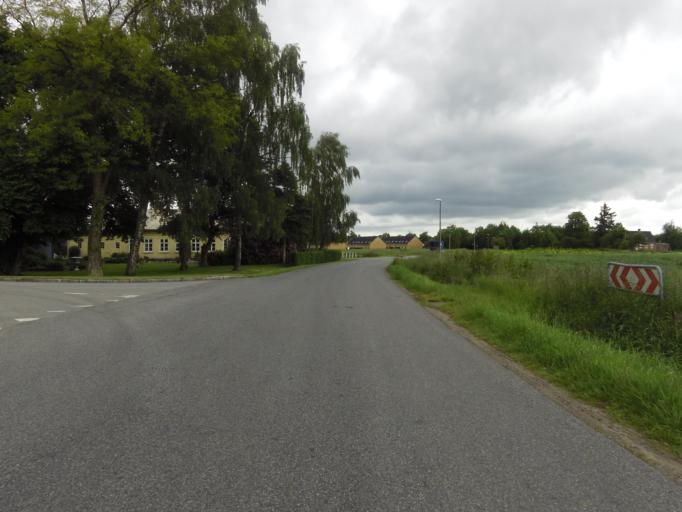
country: DK
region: South Denmark
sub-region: Haderslev Kommune
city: Gram
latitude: 55.2815
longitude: 9.0482
